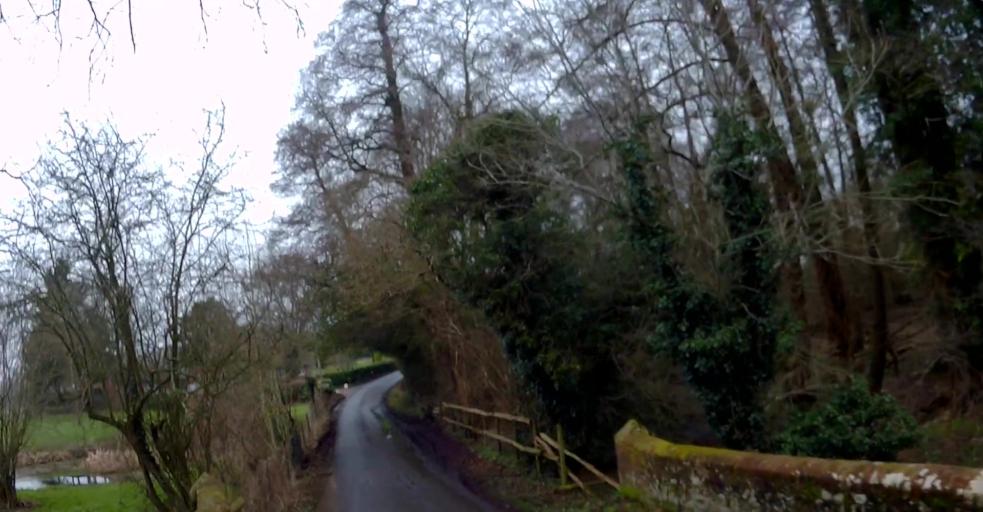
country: GB
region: England
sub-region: Hampshire
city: Eversley
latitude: 51.3333
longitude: -0.9271
